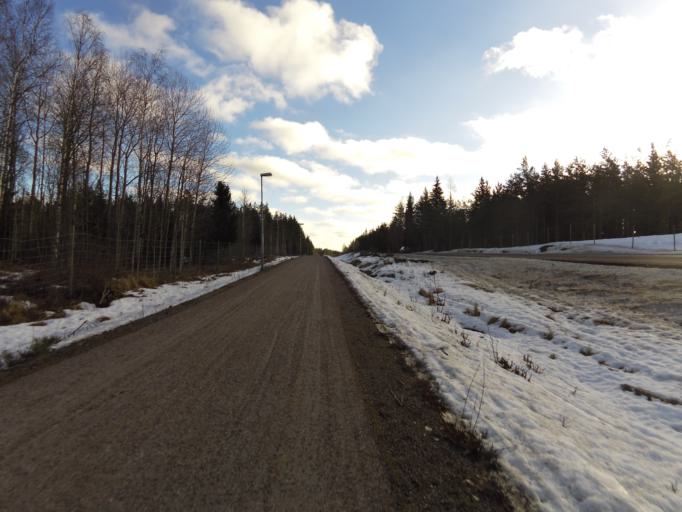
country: SE
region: Gaevleborg
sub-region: Gavle Kommun
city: Gavle
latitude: 60.6494
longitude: 17.2381
